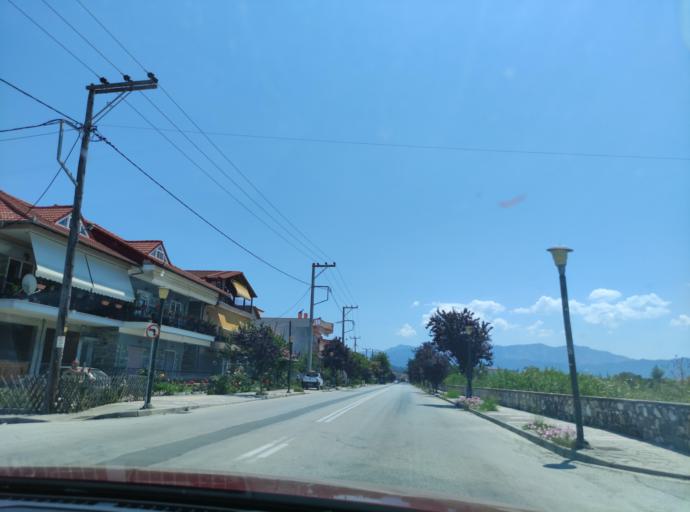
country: GR
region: East Macedonia and Thrace
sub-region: Nomos Kavalas
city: Keramoti
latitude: 40.8636
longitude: 24.7057
